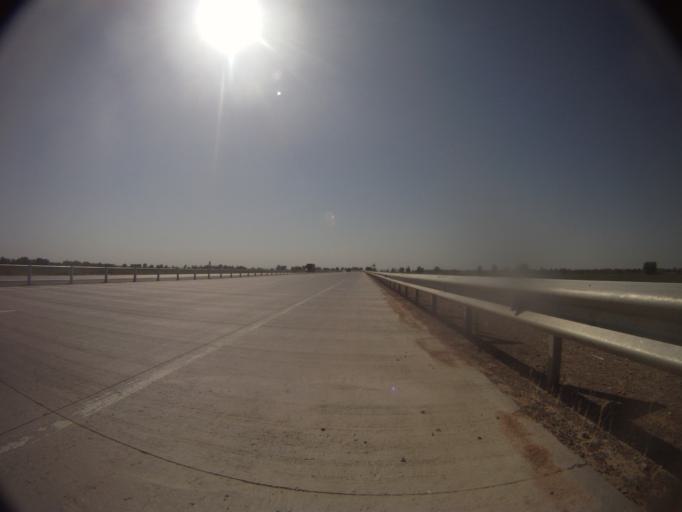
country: KZ
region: Ongtustik Qazaqstan
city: Turkestan
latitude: 43.1838
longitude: 68.4968
